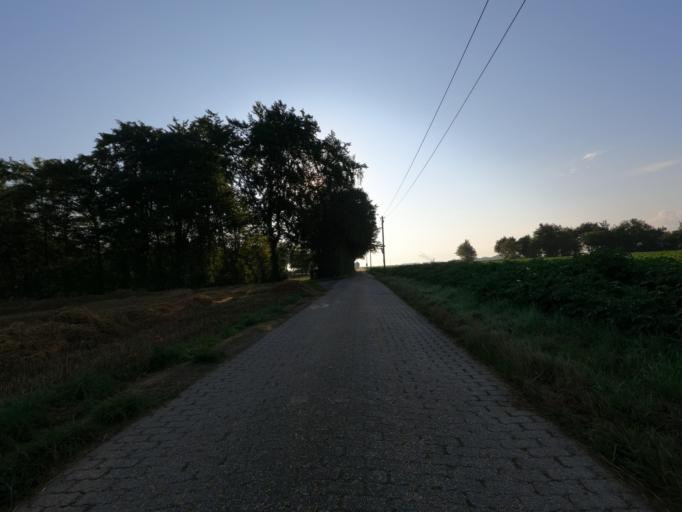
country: DE
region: North Rhine-Westphalia
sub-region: Regierungsbezirk Koln
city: Titz
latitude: 51.0181
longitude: 6.3845
